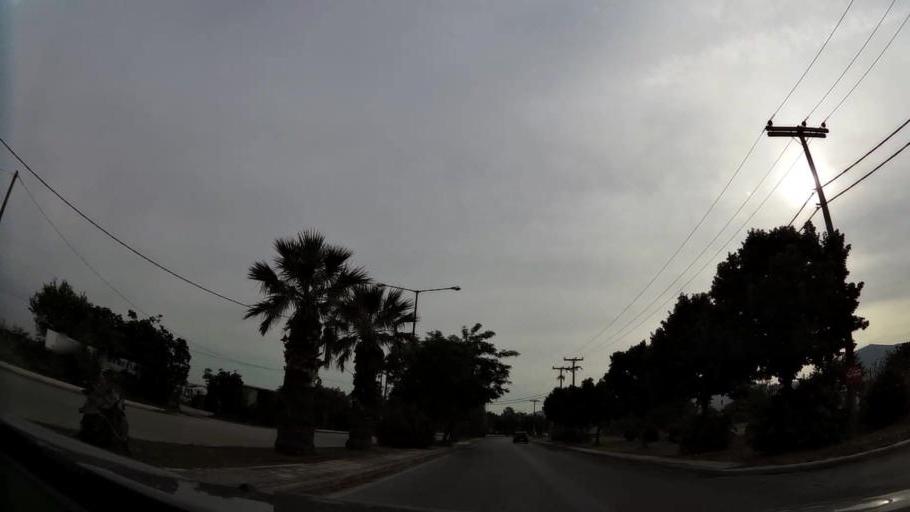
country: GR
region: Central Macedonia
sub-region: Nomos Thessalonikis
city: Thermi
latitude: 40.5400
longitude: 23.0145
